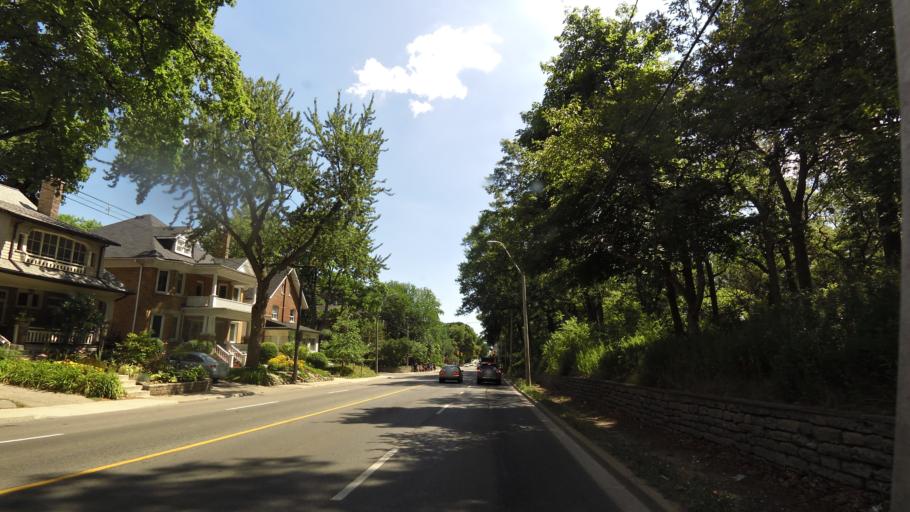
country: CA
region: Ontario
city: Toronto
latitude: 43.6465
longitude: -79.4569
